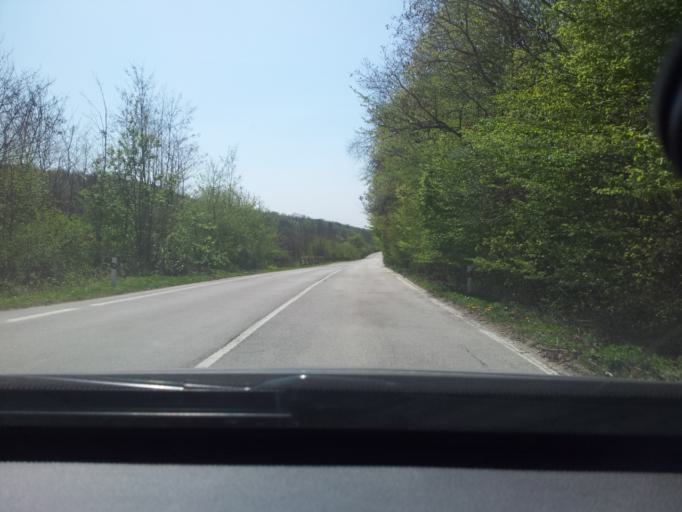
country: SK
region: Nitriansky
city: Zlate Moravce
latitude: 48.4654
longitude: 18.4124
